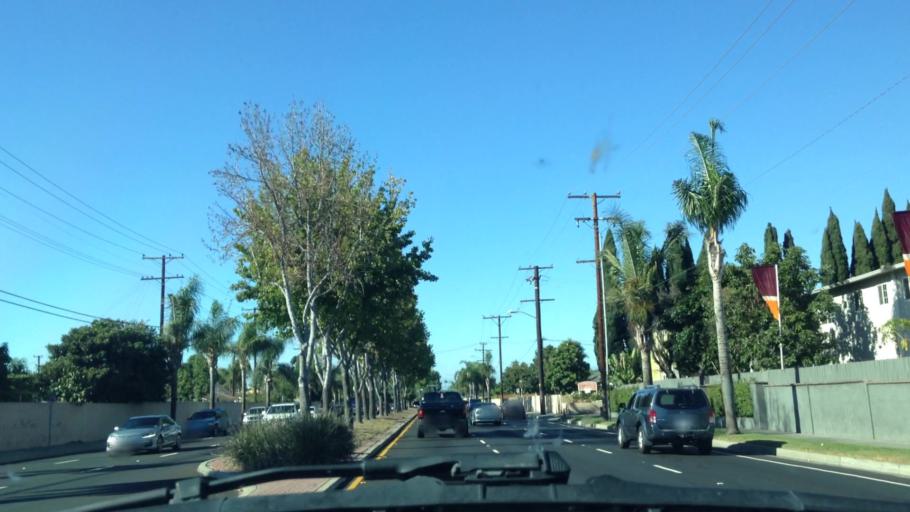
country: US
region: California
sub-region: Orange County
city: Santa Ana
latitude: 33.7374
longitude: -117.9067
